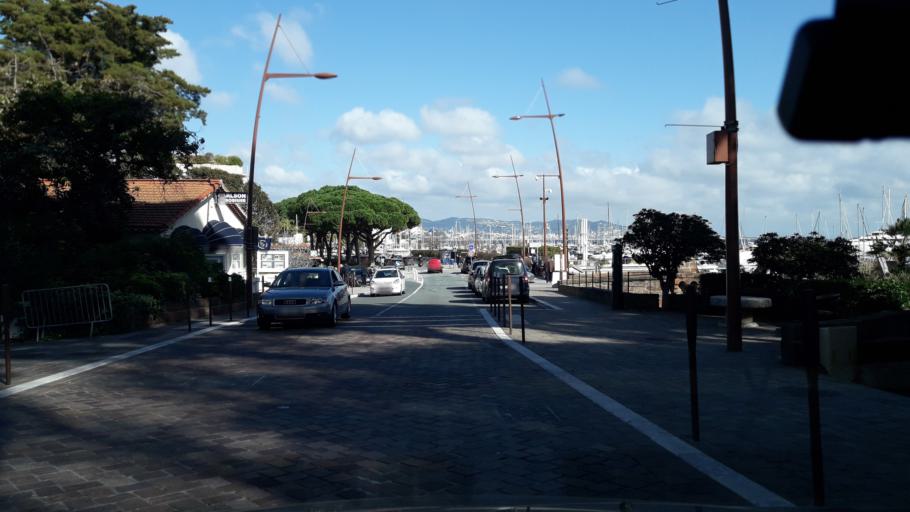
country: FR
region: Provence-Alpes-Cote d'Azur
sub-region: Departement des Alpes-Maritimes
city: Theoule-sur-Mer
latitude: 43.5241
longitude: 6.9424
